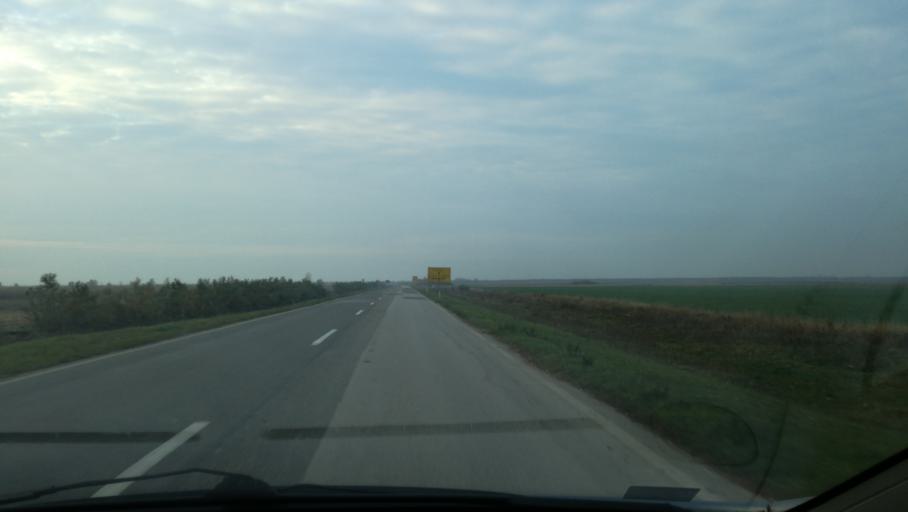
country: RS
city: Basaid
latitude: 45.6748
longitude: 20.4224
